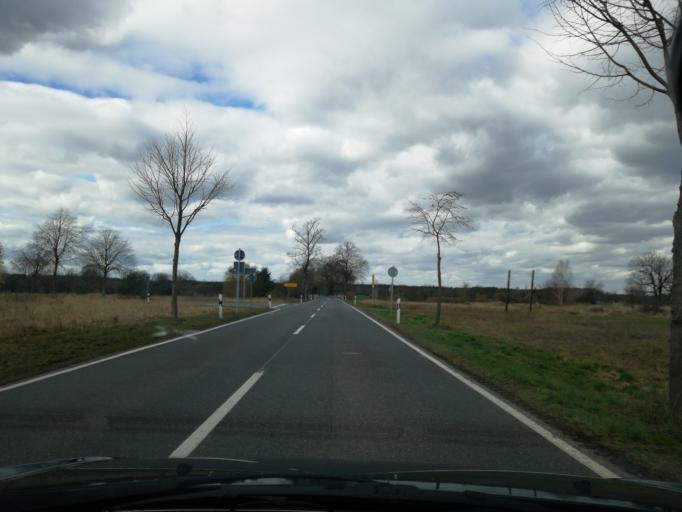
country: DE
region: Brandenburg
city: Altdobern
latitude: 51.6902
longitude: 14.0996
